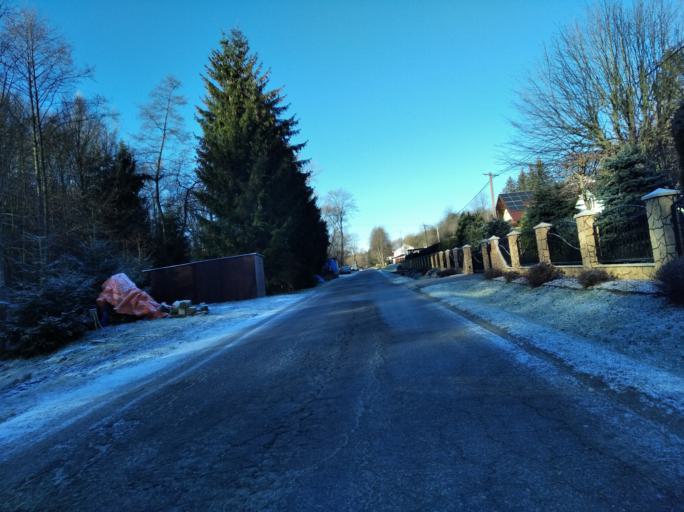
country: PL
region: Subcarpathian Voivodeship
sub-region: Powiat strzyzowski
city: Czudec
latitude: 49.9485
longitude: 21.7814
